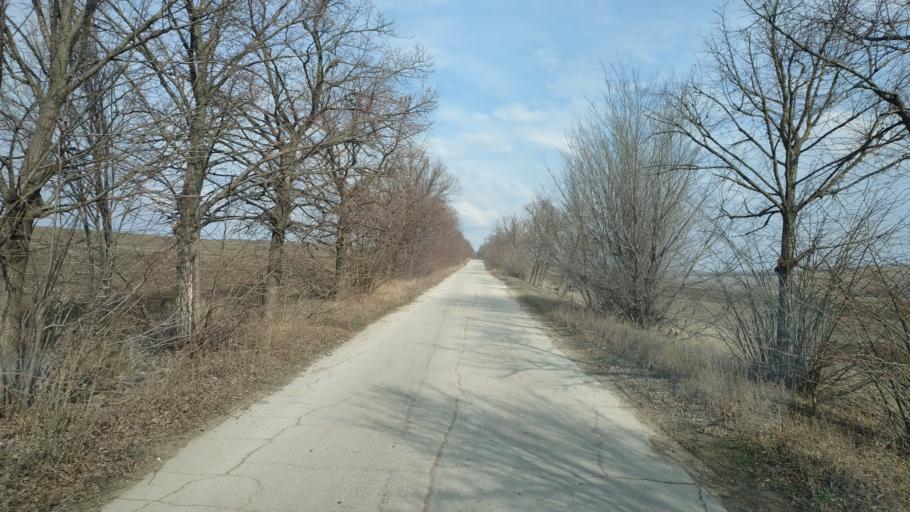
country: MD
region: Anenii Noi
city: Anenii Noi
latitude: 46.9351
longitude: 29.1073
